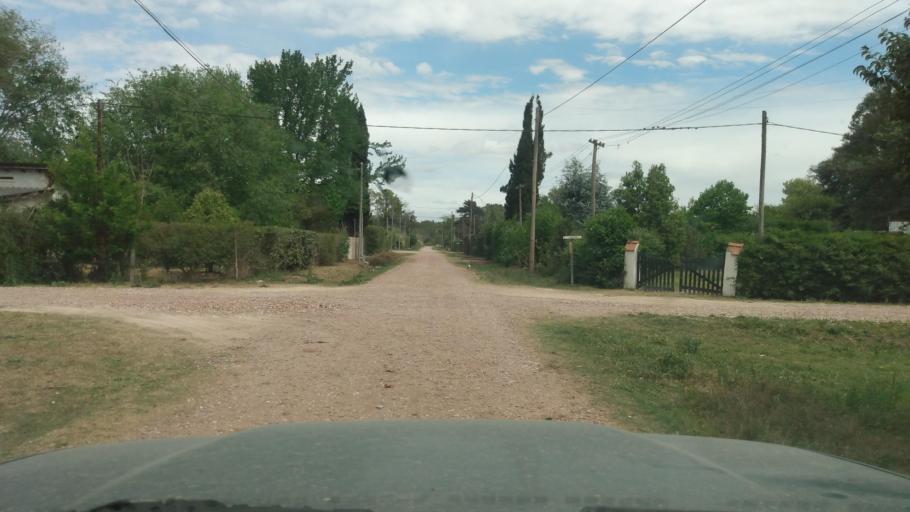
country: AR
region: Buenos Aires
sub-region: Partido de Lujan
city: Lujan
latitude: -34.5893
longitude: -59.1306
